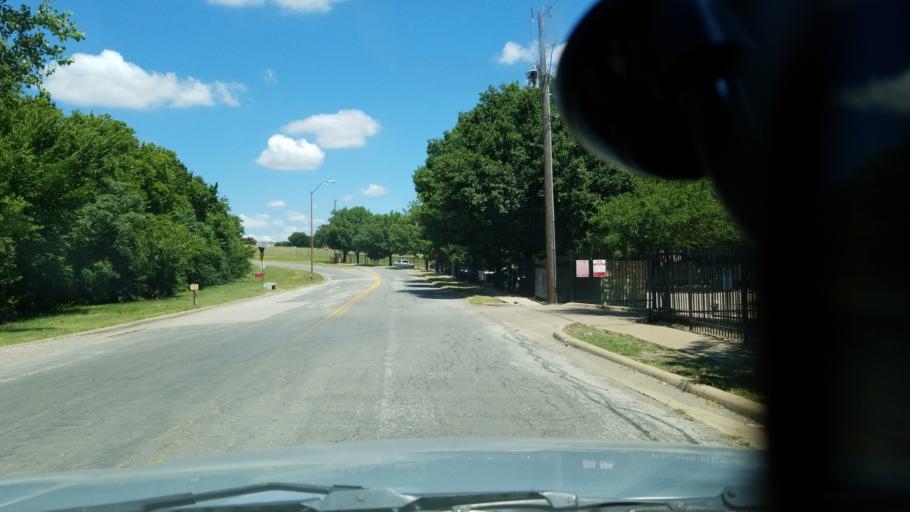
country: US
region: Texas
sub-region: Dallas County
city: Duncanville
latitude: 32.6549
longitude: -96.8731
